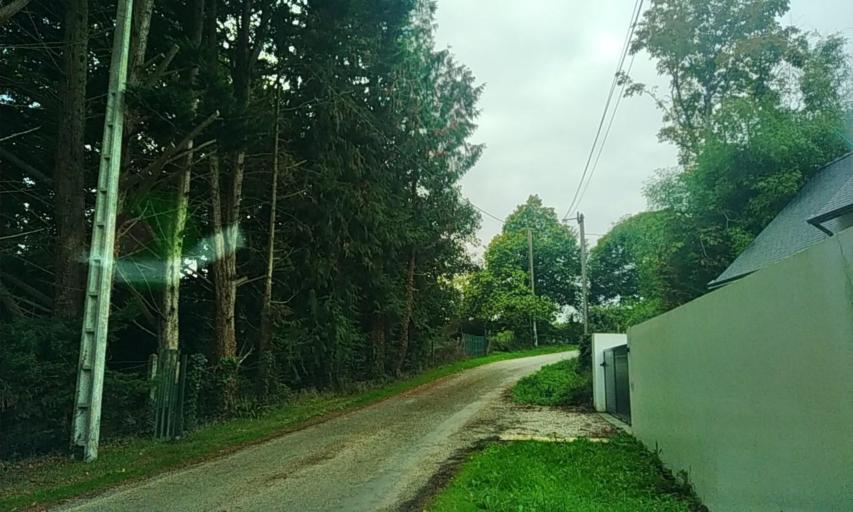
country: FR
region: Brittany
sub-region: Departement du Morbihan
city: Queven
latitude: 47.7989
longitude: -3.3825
